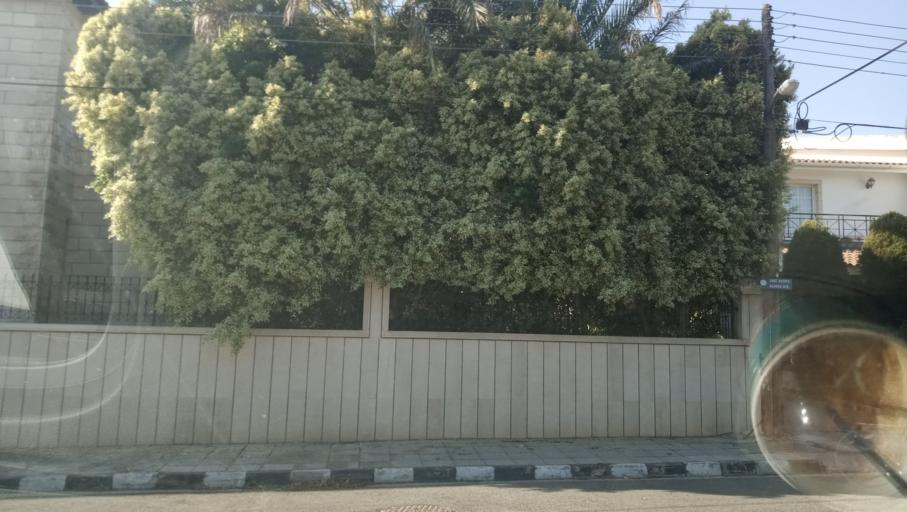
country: CY
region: Lefkosia
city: Geri
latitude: 35.1430
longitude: 33.3958
